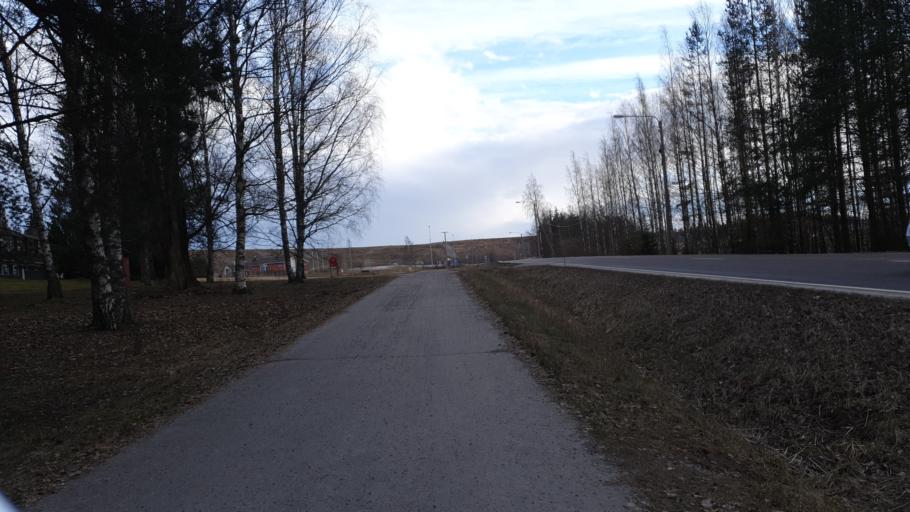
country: FI
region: Uusimaa
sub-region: Helsinki
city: Tuusula
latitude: 60.3382
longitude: 24.9211
